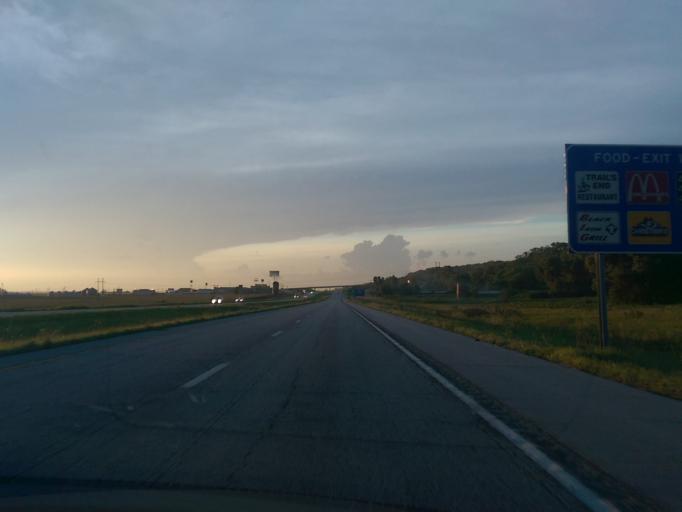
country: US
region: Missouri
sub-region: Atchison County
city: Rock Port
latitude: 40.3978
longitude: -95.5501
